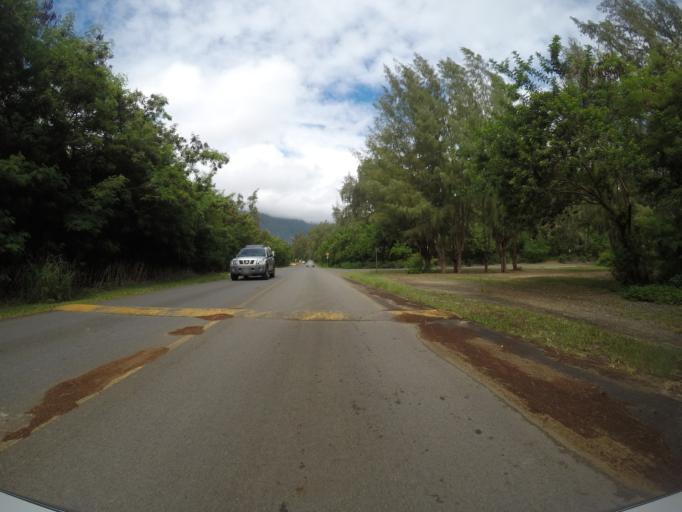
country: US
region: Hawaii
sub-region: Honolulu County
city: Waimanalo Beach
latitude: 21.3444
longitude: -157.7046
